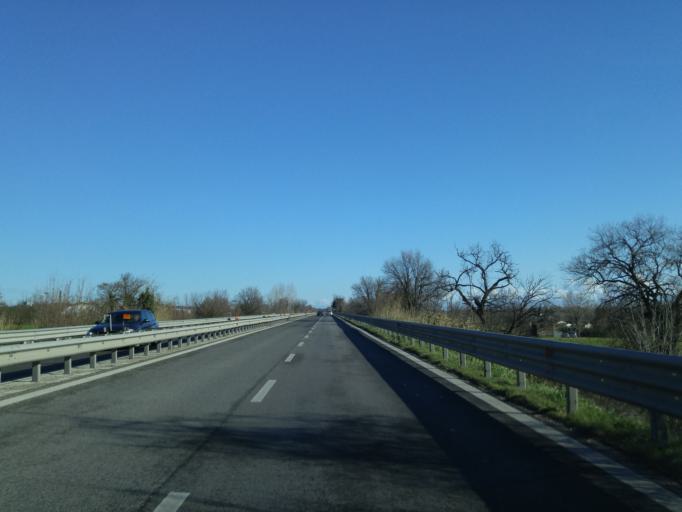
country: IT
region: The Marches
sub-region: Provincia di Pesaro e Urbino
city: Calcinelli
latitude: 43.7536
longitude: 12.9291
